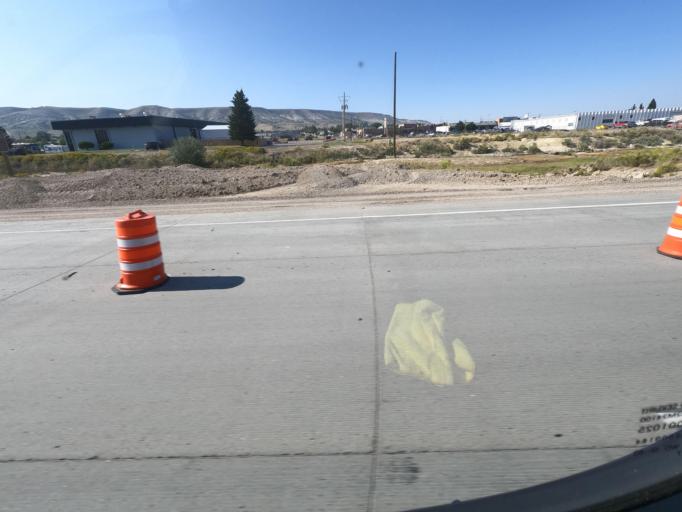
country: US
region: Wyoming
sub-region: Sweetwater County
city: Rock Springs
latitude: 41.5759
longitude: -109.2648
